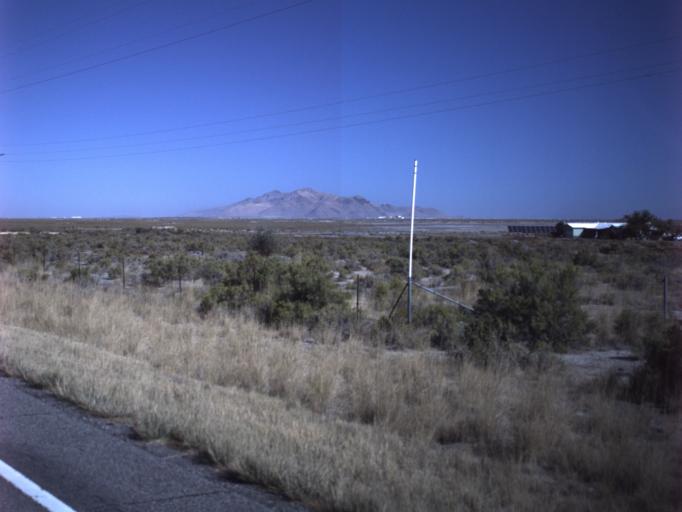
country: US
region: Utah
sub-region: Tooele County
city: Grantsville
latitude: 40.6446
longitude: -112.5272
